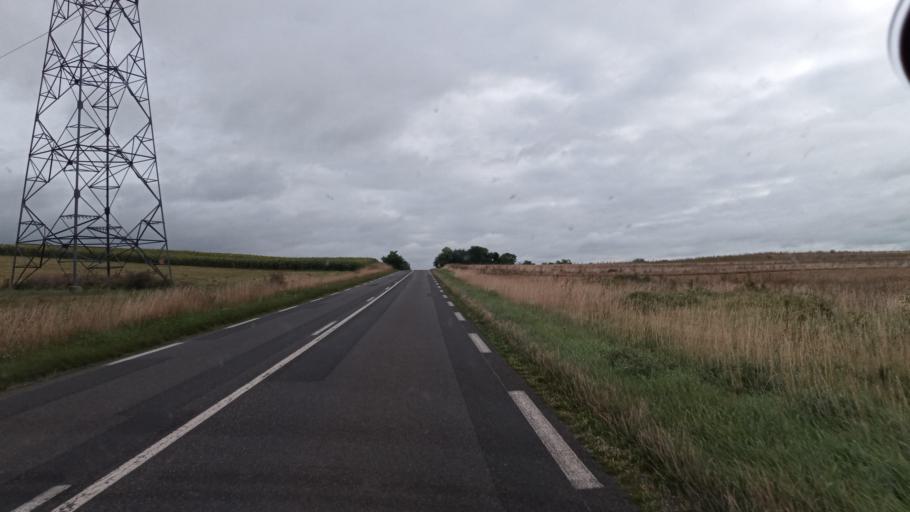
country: FR
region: Ile-de-France
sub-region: Departement de Seine-et-Marne
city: Cannes-Ecluse
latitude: 48.3306
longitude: 2.9565
